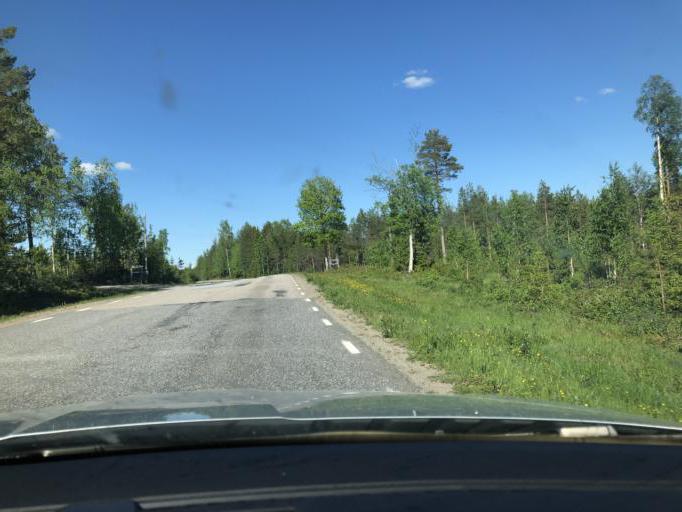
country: SE
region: Norrbotten
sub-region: Kalix Kommun
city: Kalix
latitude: 65.8884
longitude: 23.1526
